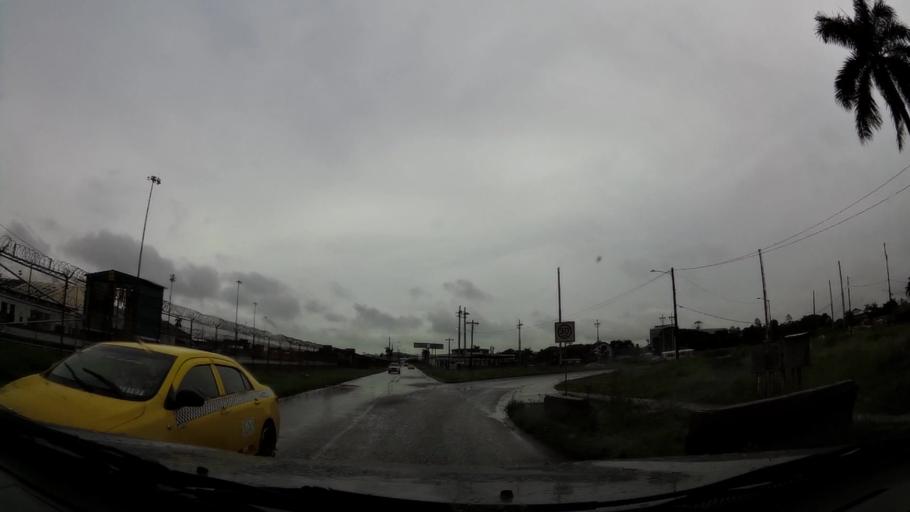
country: PA
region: Colon
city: Arco Iris
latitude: 9.3400
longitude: -79.8976
